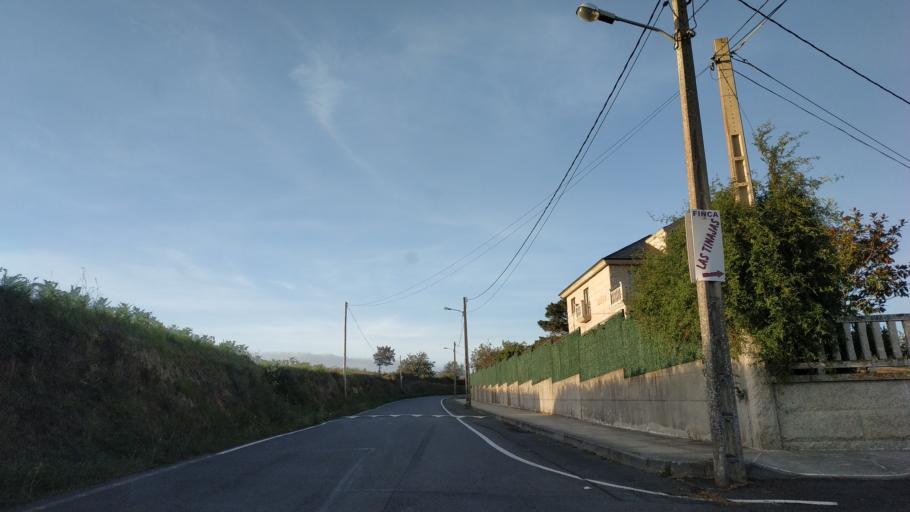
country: ES
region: Galicia
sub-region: Provincia da Coruna
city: Oleiros
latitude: 43.3567
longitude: -8.3440
